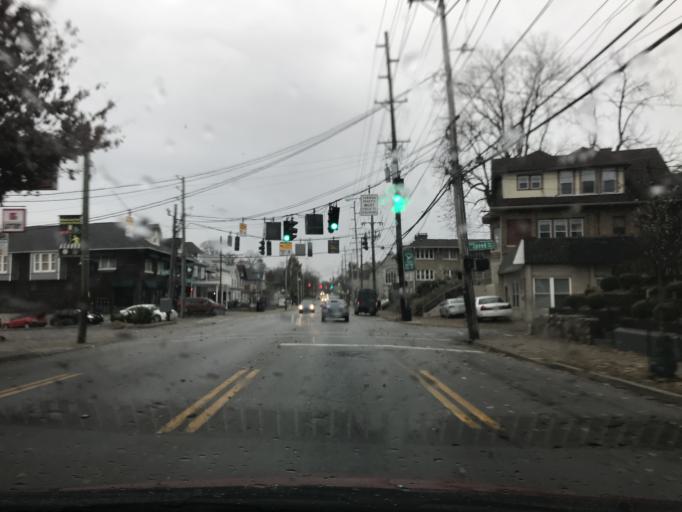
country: US
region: Kentucky
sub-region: Jefferson County
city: Audubon Park
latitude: 38.2287
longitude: -85.7015
